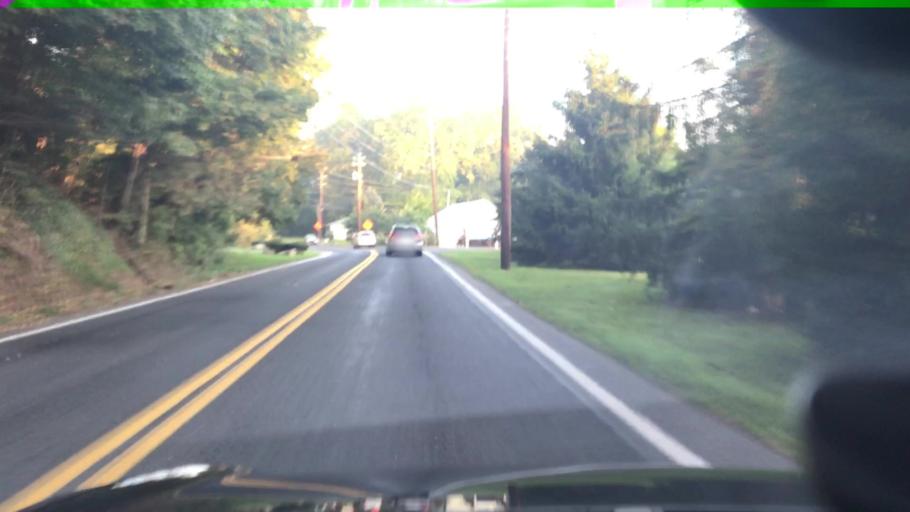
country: US
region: Pennsylvania
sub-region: Cumberland County
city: Lower Allen
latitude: 40.1759
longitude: -76.9241
